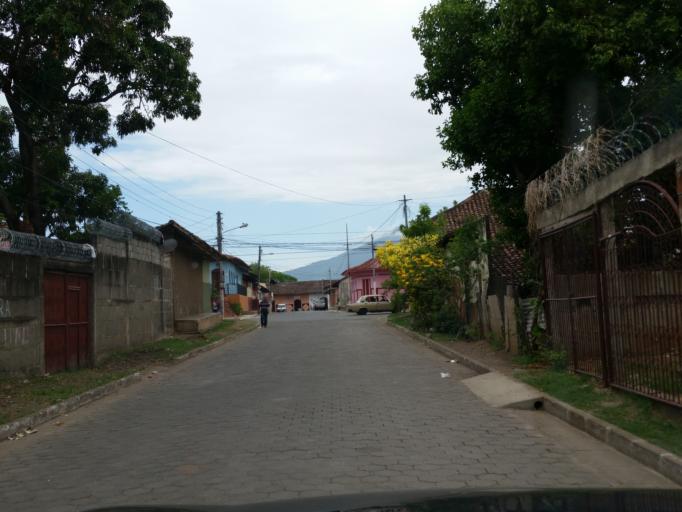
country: NI
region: Granada
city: Granada
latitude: 11.9324
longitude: -85.9601
